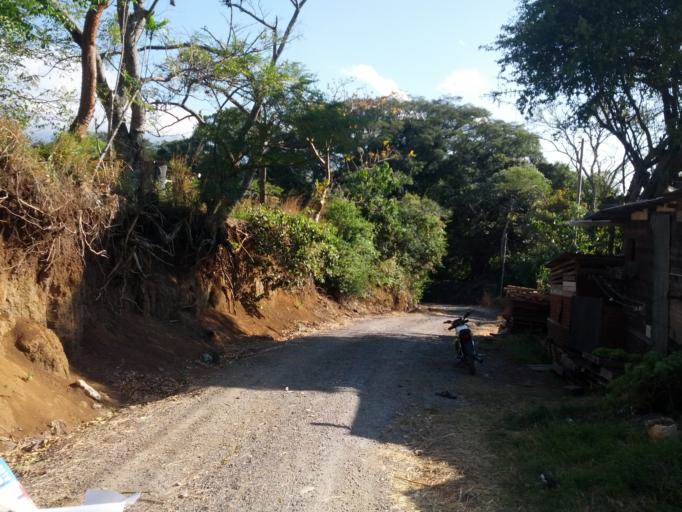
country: CR
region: Alajuela
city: Alajuela
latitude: 9.9905
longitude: -84.2123
